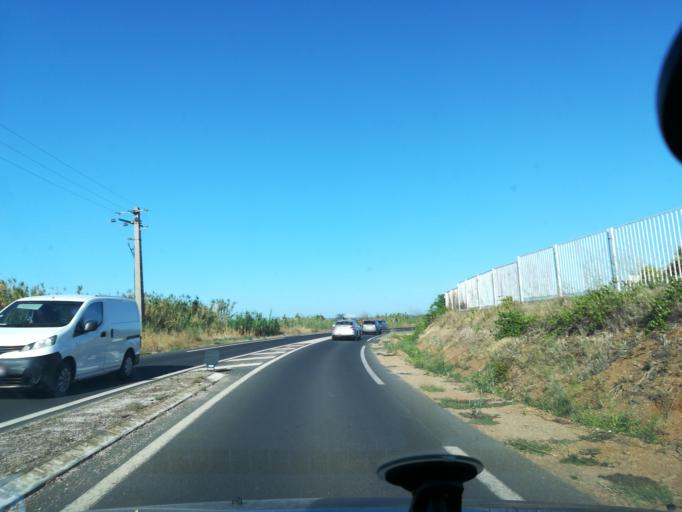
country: FR
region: Languedoc-Roussillon
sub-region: Departement de l'Herault
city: Portiragnes
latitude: 43.2979
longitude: 3.3441
